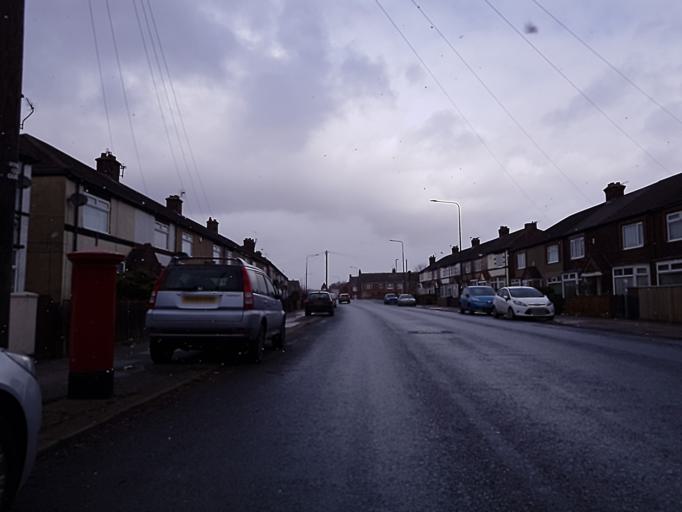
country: GB
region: England
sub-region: North East Lincolnshire
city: Grimbsy
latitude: 53.5702
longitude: -0.0988
